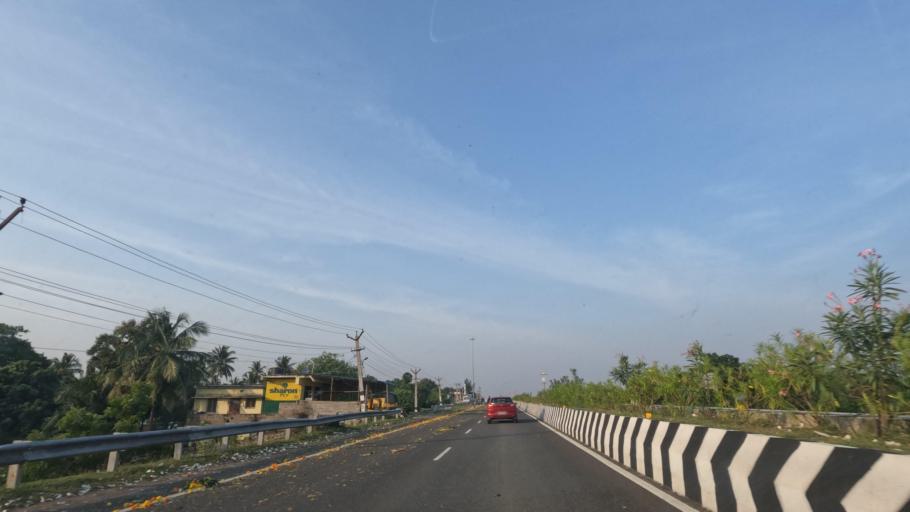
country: IN
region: Tamil Nadu
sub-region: Kancheepuram
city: Mamallapuram
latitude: 12.7246
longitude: 80.2306
